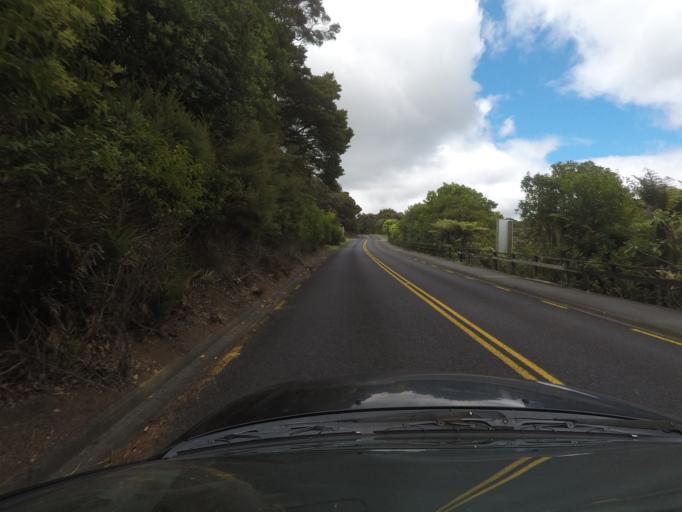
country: NZ
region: Northland
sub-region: Far North District
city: Paihia
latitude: -35.2876
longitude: 174.0962
